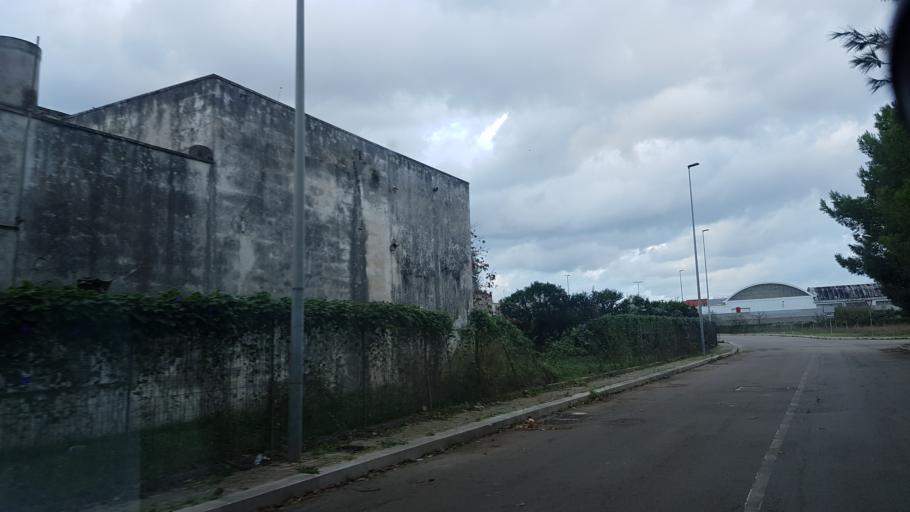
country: IT
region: Apulia
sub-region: Provincia di Brindisi
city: San Pietro Vernotico
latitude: 40.4899
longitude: 18.0018
